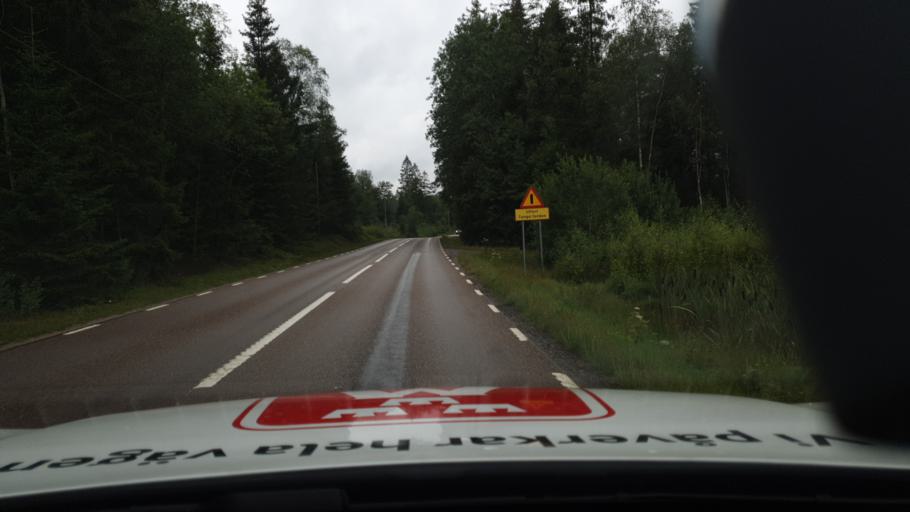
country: SE
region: Vaestra Goetaland
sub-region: Uddevalla Kommun
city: Ljungskile
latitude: 58.1759
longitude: 11.9997
